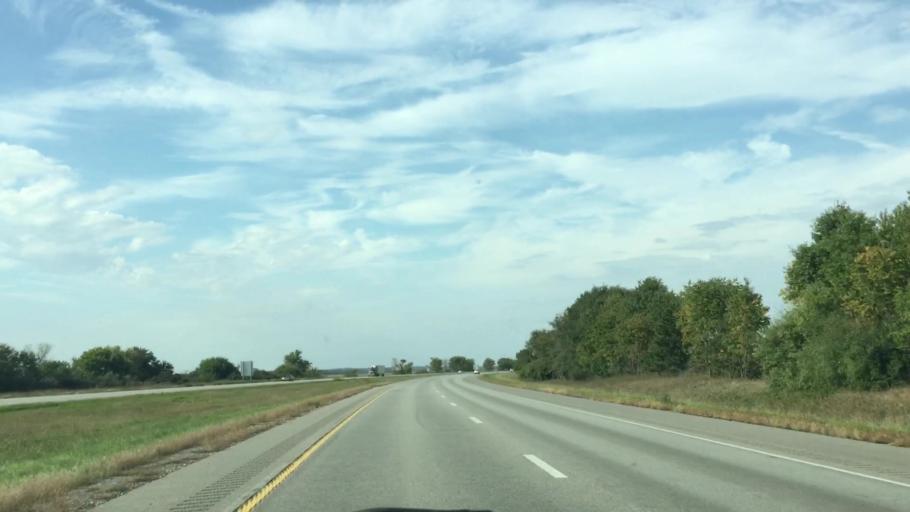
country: US
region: Illinois
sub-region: Rock Island County
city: Port Byron
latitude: 41.5463
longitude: -90.2565
